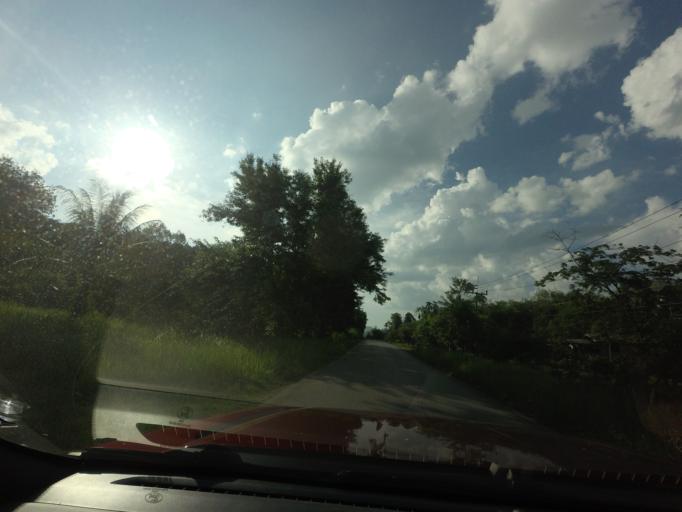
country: TH
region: Yala
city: Ban Nang Sata
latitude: 6.2143
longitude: 101.2326
